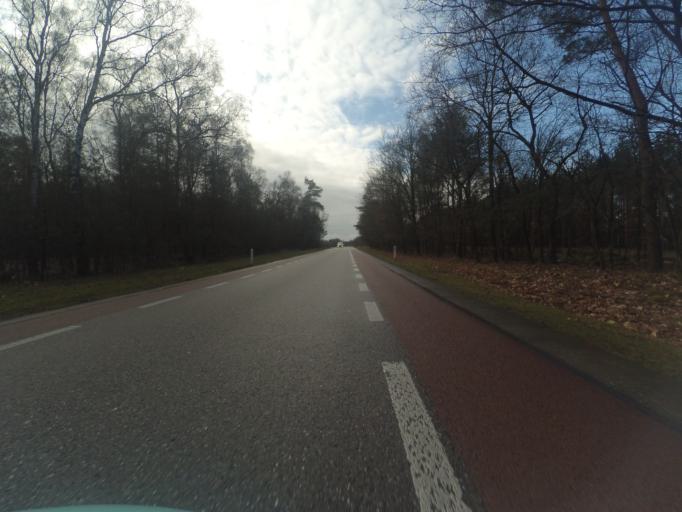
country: NL
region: Gelderland
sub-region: Gemeente Arnhem
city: Hoogkamp
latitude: 52.0802
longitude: 5.8801
